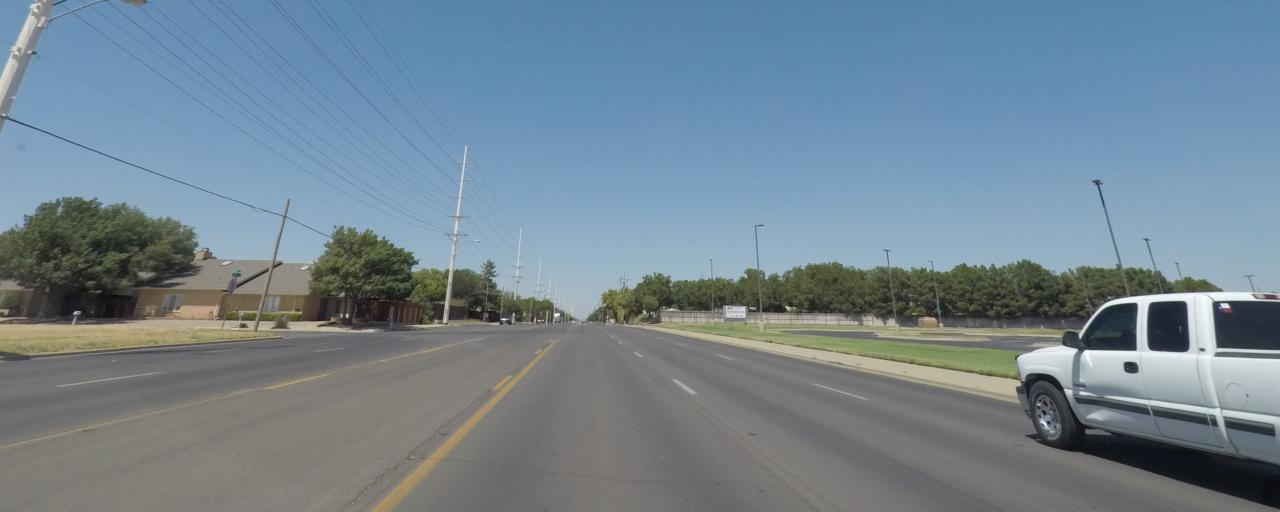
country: US
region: Texas
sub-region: Lubbock County
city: Lubbock
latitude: 33.5072
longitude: -101.8876
